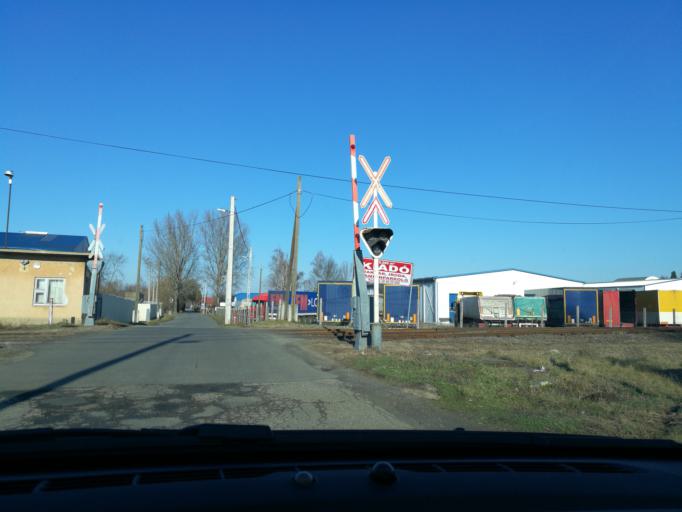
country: HU
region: Szabolcs-Szatmar-Bereg
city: Nyiregyhaza
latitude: 47.9428
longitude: 21.7466
